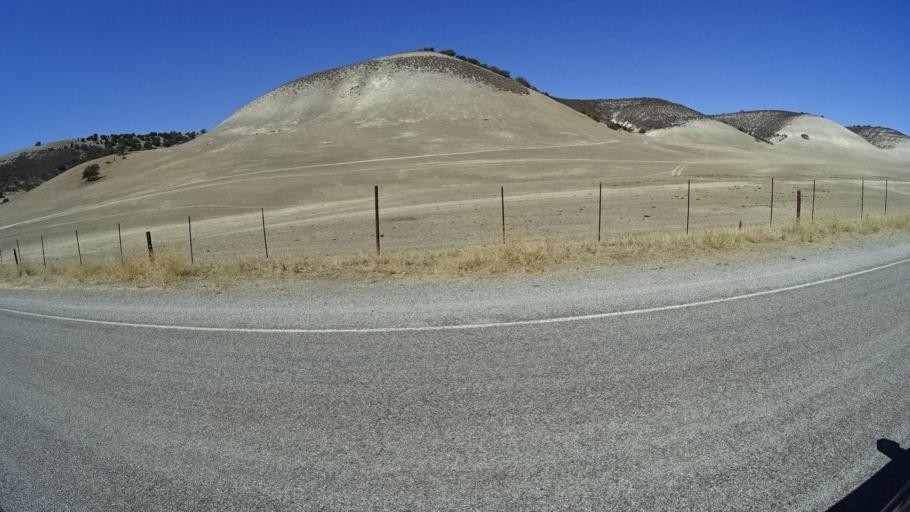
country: US
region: California
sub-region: Monterey County
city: King City
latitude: 36.3111
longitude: -121.0417
